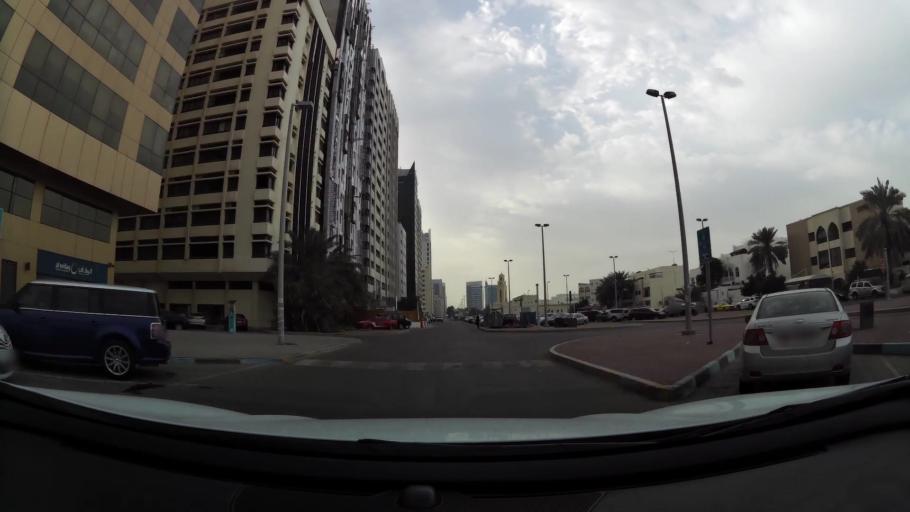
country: AE
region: Abu Dhabi
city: Abu Dhabi
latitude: 24.4665
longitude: 54.3731
